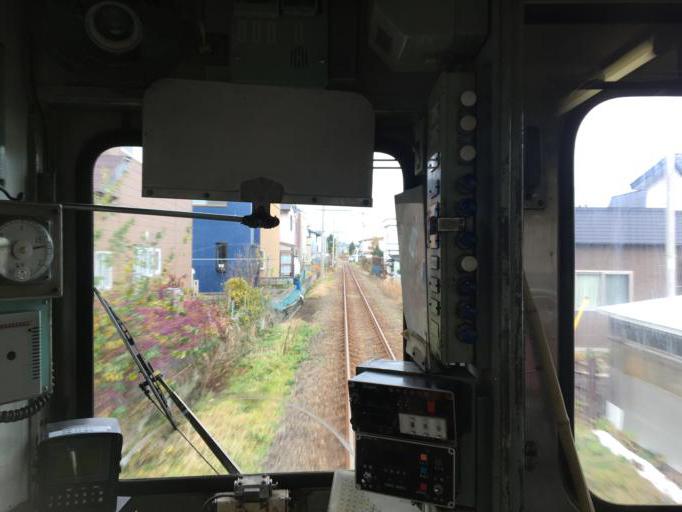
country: JP
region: Aomori
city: Hirosaki
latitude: 40.5701
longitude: 140.4771
